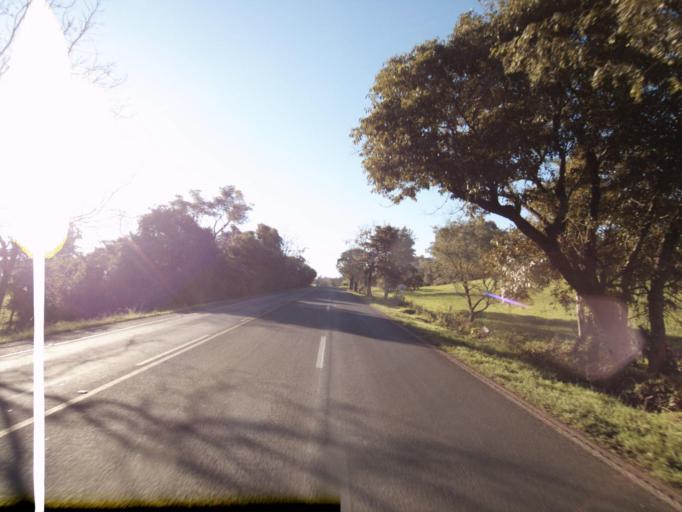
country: BR
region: Santa Catarina
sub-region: Chapeco
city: Chapeco
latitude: -26.9065
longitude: -52.8670
